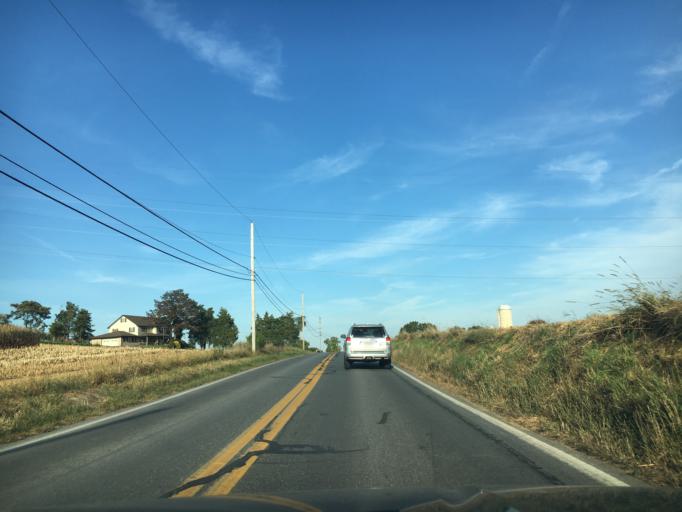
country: US
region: Pennsylvania
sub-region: Lancaster County
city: Brownstown
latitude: 40.1255
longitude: -76.1900
